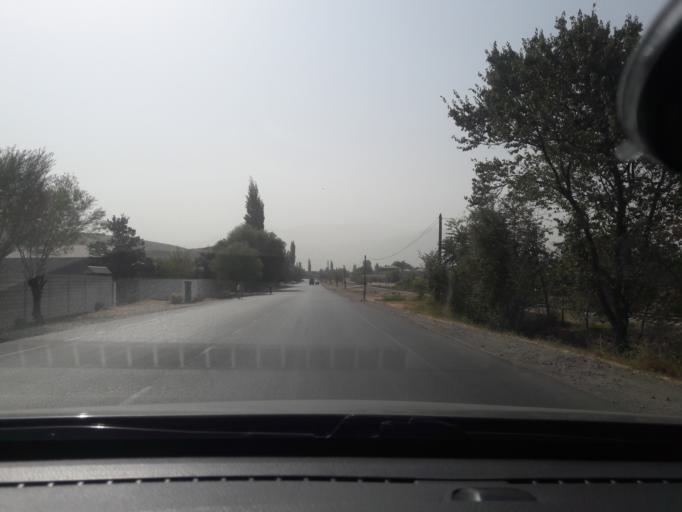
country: TJ
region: Republican Subordination
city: Vahdat
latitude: 38.5246
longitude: 69.0276
